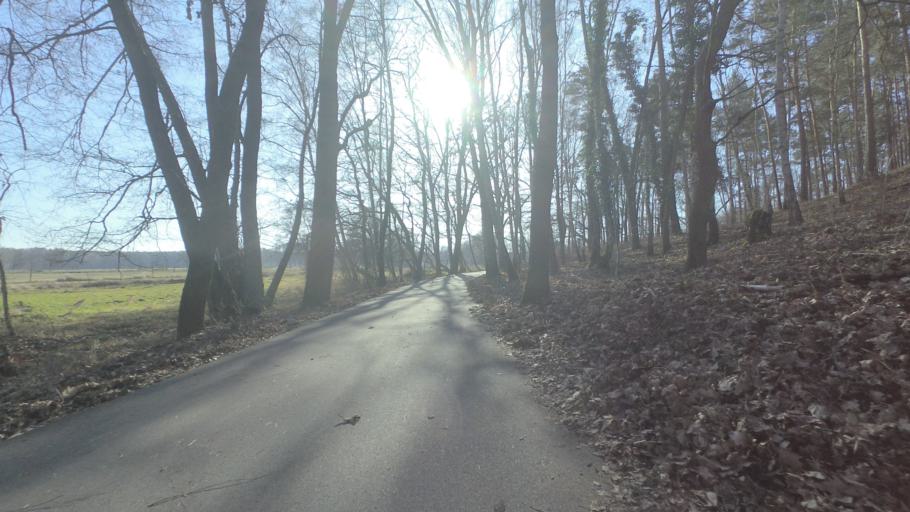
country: DE
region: Brandenburg
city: Luckenwalde
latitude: 52.0711
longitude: 13.1677
